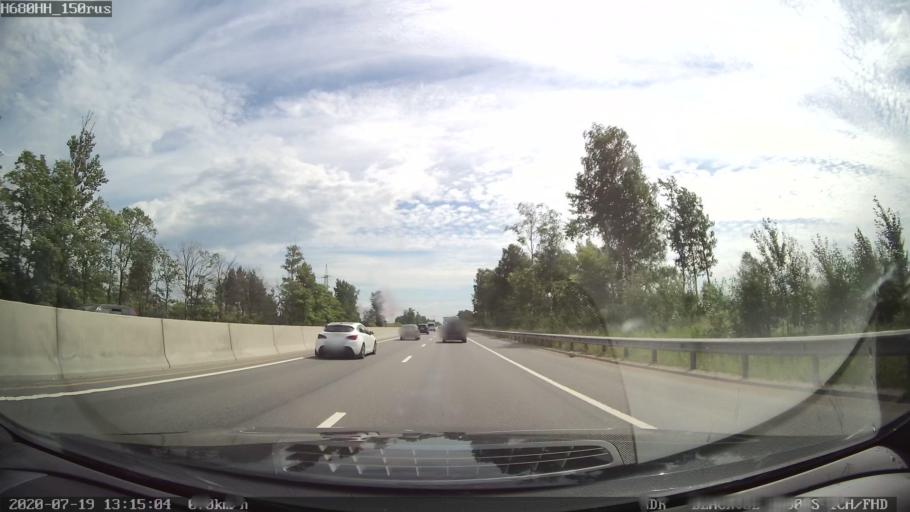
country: RU
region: St.-Petersburg
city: Kolpino
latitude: 59.7284
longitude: 30.5341
